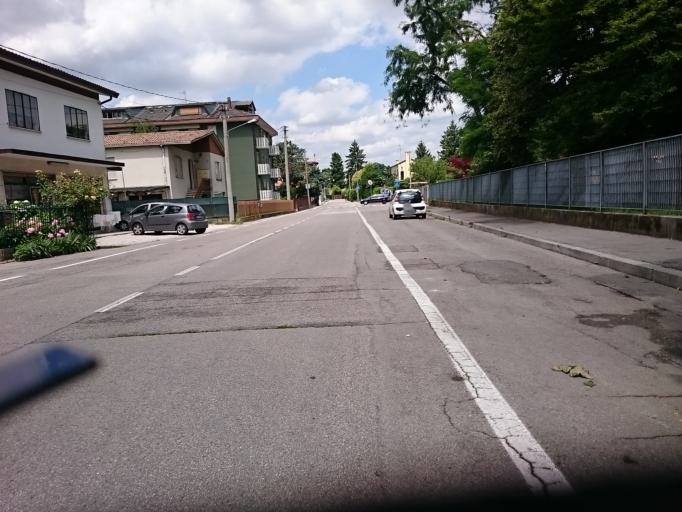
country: IT
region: Veneto
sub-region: Provincia di Padova
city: Ponte San Nicolo
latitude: 45.3822
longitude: 11.8988
